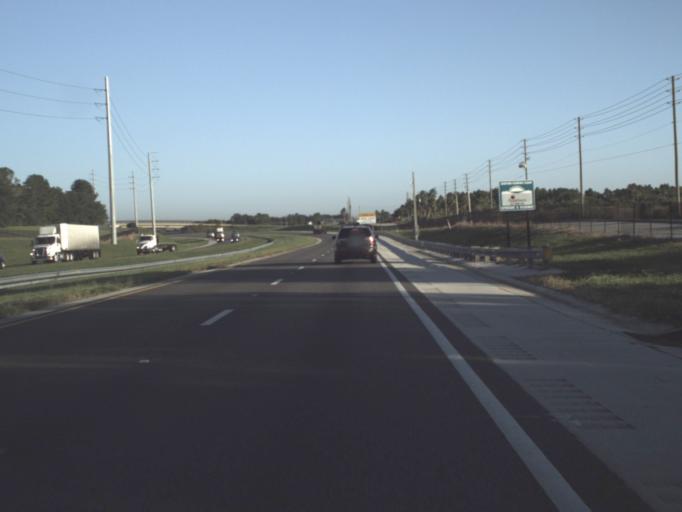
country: US
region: Florida
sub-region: Polk County
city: Citrus Ridge
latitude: 28.3123
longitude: -81.6073
